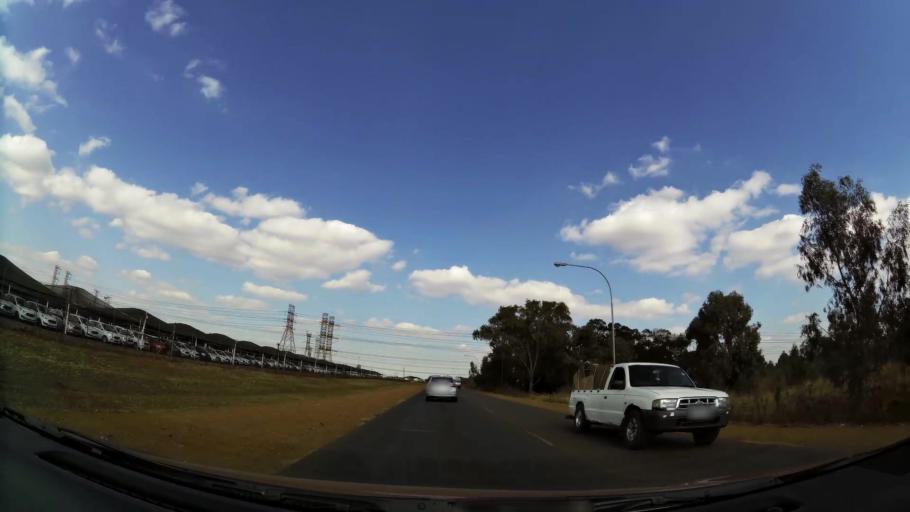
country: ZA
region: Gauteng
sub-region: Ekurhuleni Metropolitan Municipality
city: Tembisa
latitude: -26.0109
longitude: 28.2522
